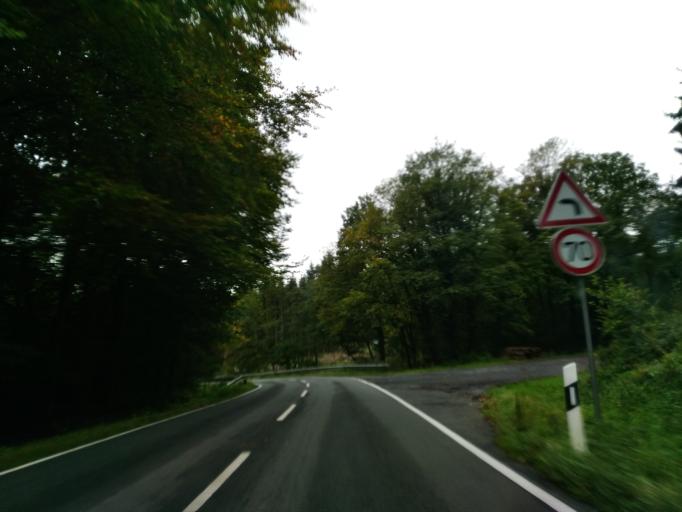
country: DE
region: North Rhine-Westphalia
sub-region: Regierungsbezirk Koln
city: Bad Honnef
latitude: 50.6687
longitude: 7.2858
